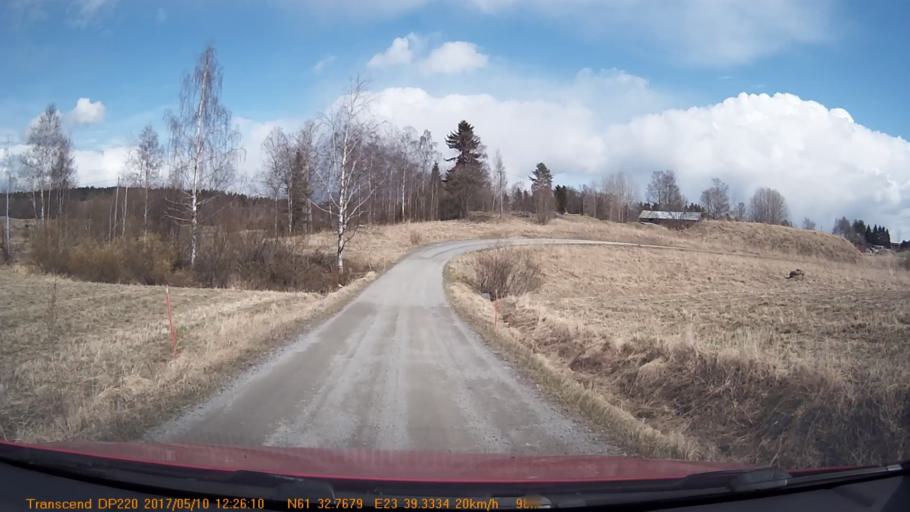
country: FI
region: Pirkanmaa
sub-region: Tampere
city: Yloejaervi
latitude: 61.5463
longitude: 23.6559
